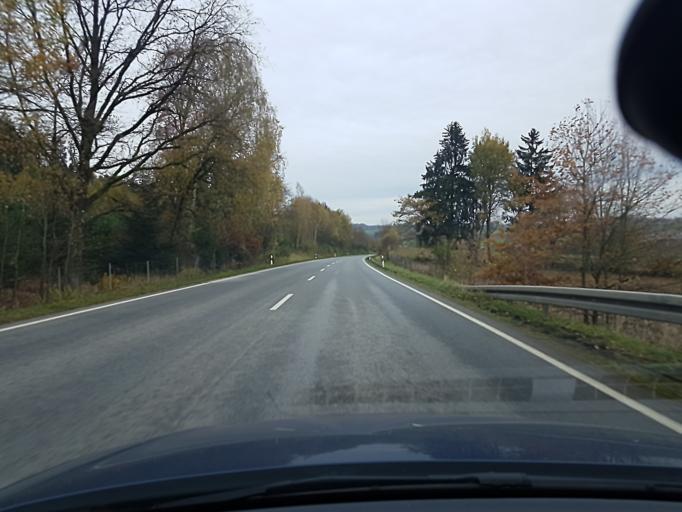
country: DE
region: Bavaria
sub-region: Lower Bavaria
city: Mallersdorf-Pfaffenberg
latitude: 48.7661
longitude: 12.1910
